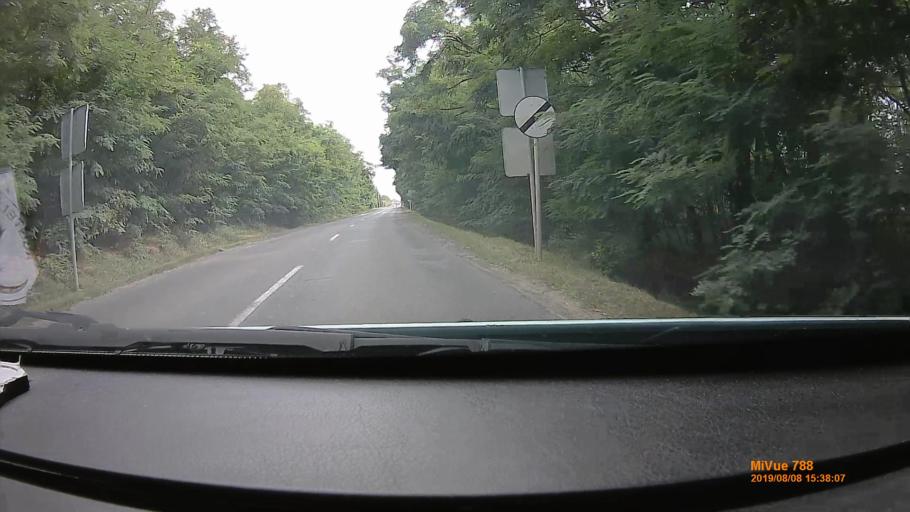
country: HU
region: Szabolcs-Szatmar-Bereg
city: Kocsord
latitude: 47.9451
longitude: 22.4273
